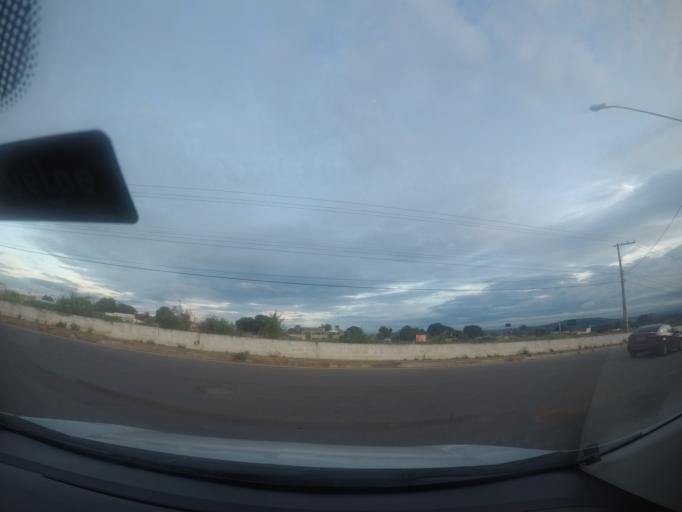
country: BR
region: Goias
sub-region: Goiania
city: Goiania
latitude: -16.7214
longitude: -49.3719
